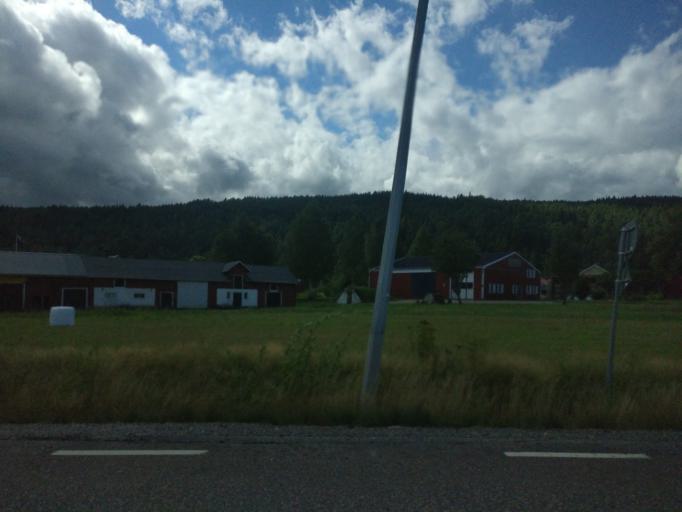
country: SE
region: Vaermland
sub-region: Hagfors Kommun
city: Ekshaerad
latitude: 60.2871
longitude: 13.3978
